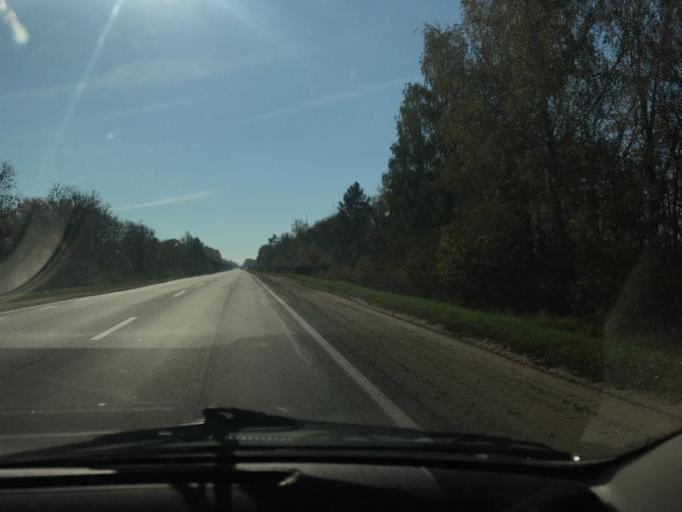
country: BY
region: Minsk
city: Starobin
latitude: 52.7953
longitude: 27.4645
